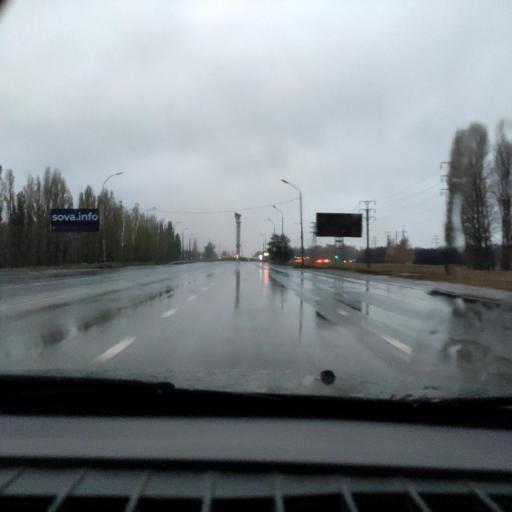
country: RU
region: Samara
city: Tol'yatti
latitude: 53.5563
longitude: 49.2883
